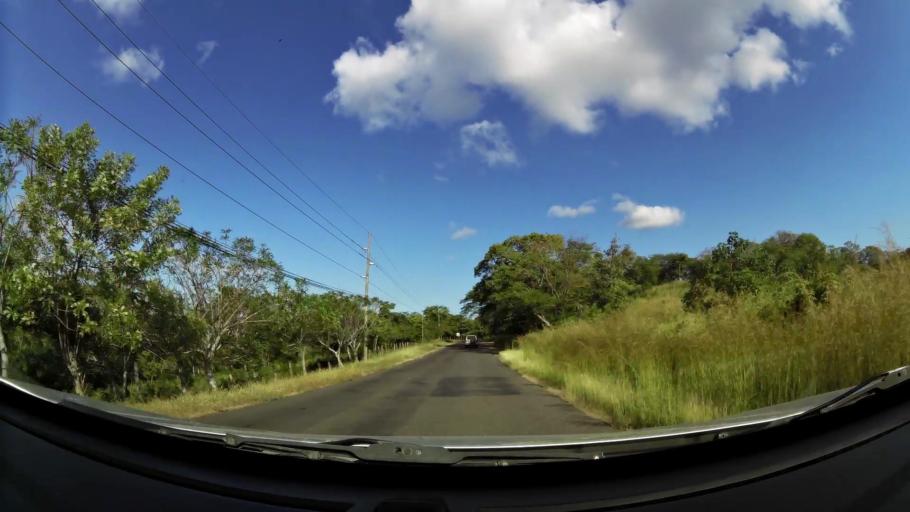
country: CR
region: Guanacaste
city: Sardinal
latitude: 10.5407
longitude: -85.6731
